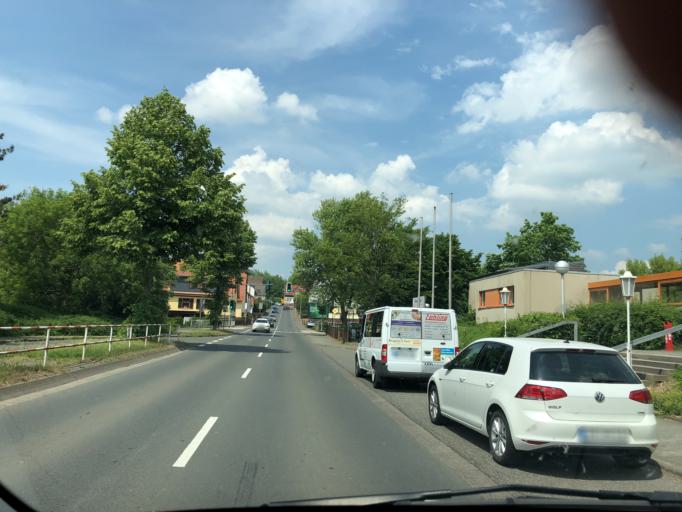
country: DE
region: Hesse
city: Neustadt (Hessen)
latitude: 50.8496
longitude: 9.1099
